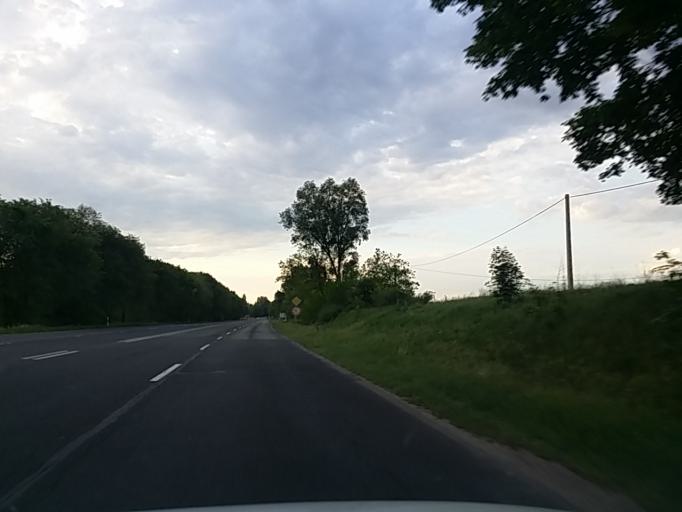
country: HU
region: Bacs-Kiskun
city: Kecskemet
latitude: 46.9707
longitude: 19.6339
